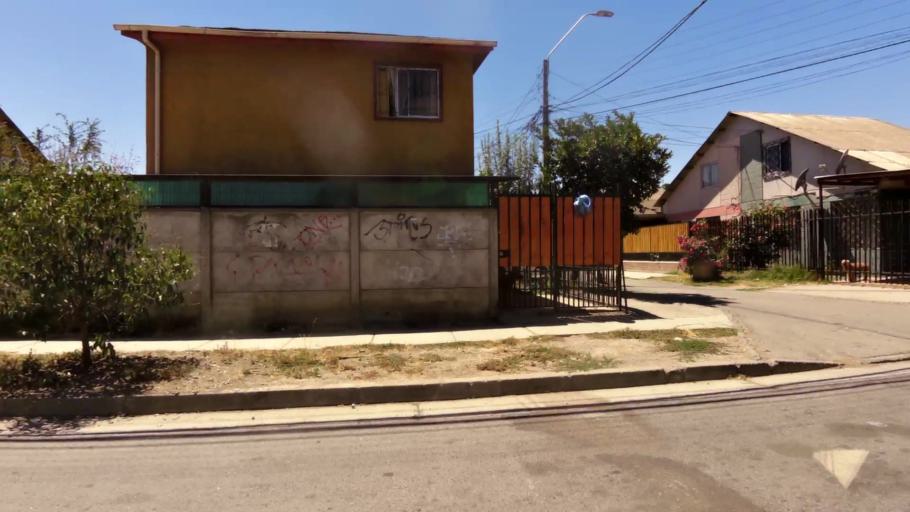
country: CL
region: O'Higgins
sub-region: Provincia de Cachapoal
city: Rancagua
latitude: -34.1559
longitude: -70.7530
